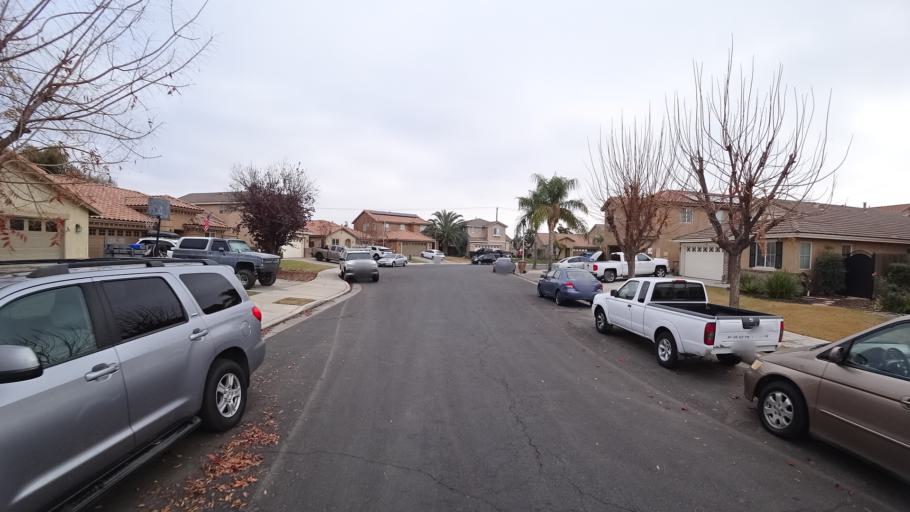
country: US
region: California
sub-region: Kern County
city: Greenfield
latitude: 35.2999
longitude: -119.0757
